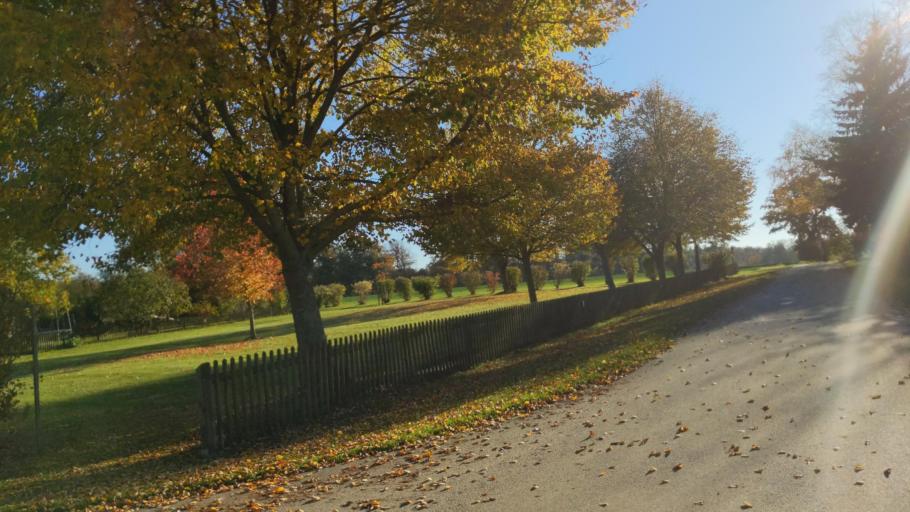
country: DE
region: Schleswig-Holstein
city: Gross Gronau
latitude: 53.7868
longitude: 10.7475
